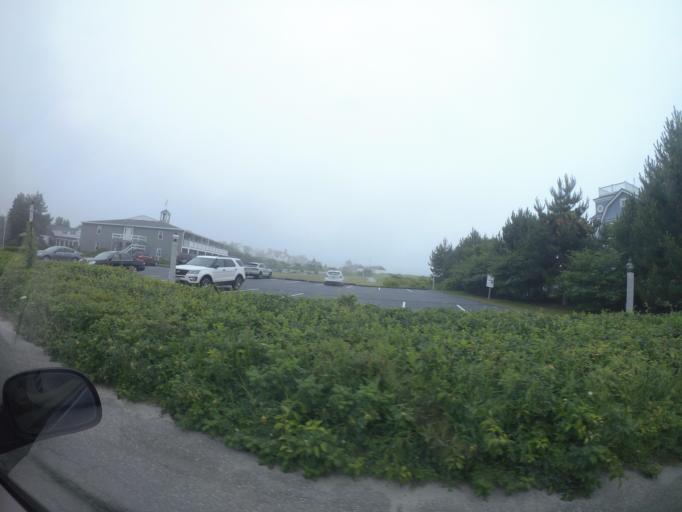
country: US
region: Maine
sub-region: York County
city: Kennebunkport
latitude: 43.3485
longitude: -70.4801
